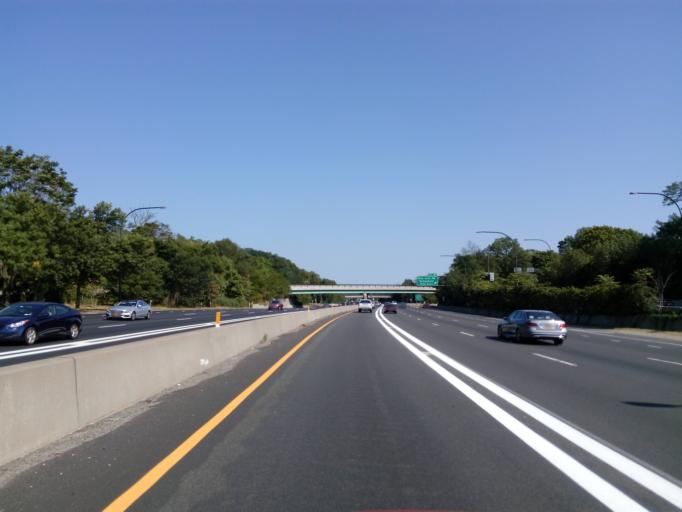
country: US
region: New York
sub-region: Nassau County
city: East Hills
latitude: 40.7843
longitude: -73.6288
